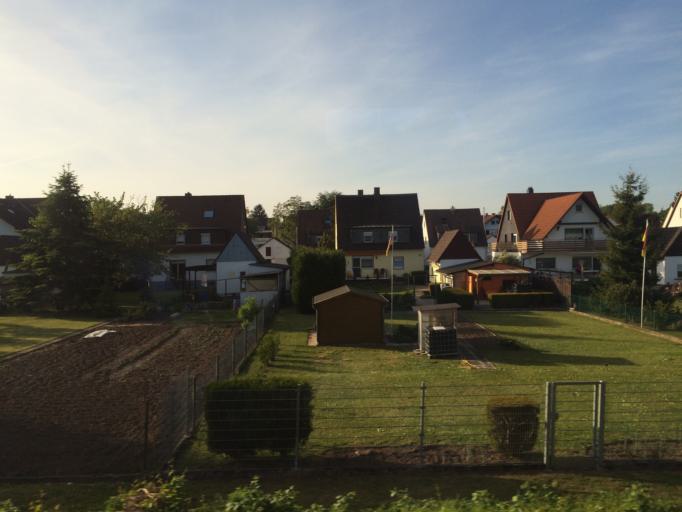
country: DE
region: Hesse
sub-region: Regierungsbezirk Darmstadt
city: Russelsheim
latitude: 50.0014
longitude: 8.4002
